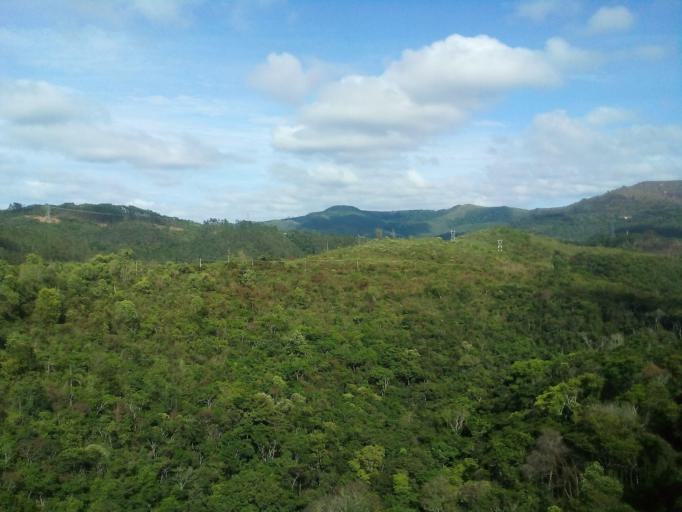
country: BR
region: Minas Gerais
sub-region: Raposos
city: Raposos
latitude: -19.8813
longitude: -43.7655
